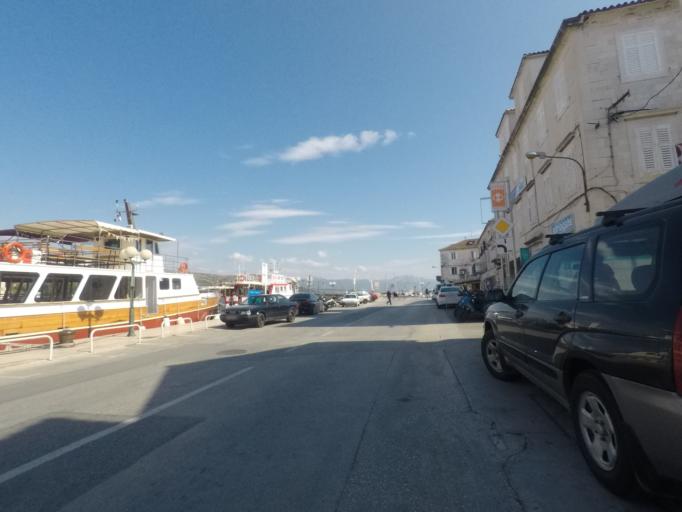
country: HR
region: Splitsko-Dalmatinska
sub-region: Grad Trogir
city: Trogir
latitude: 43.5148
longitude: 16.2515
